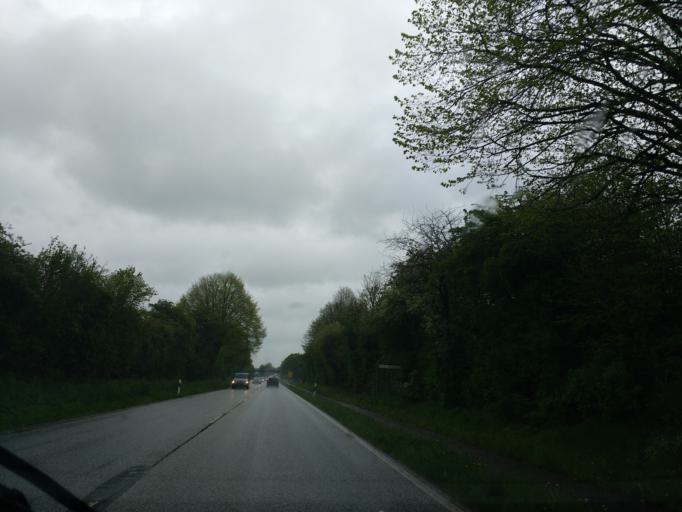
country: DE
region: Schleswig-Holstein
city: Barkelsby
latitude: 54.4968
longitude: 9.8439
